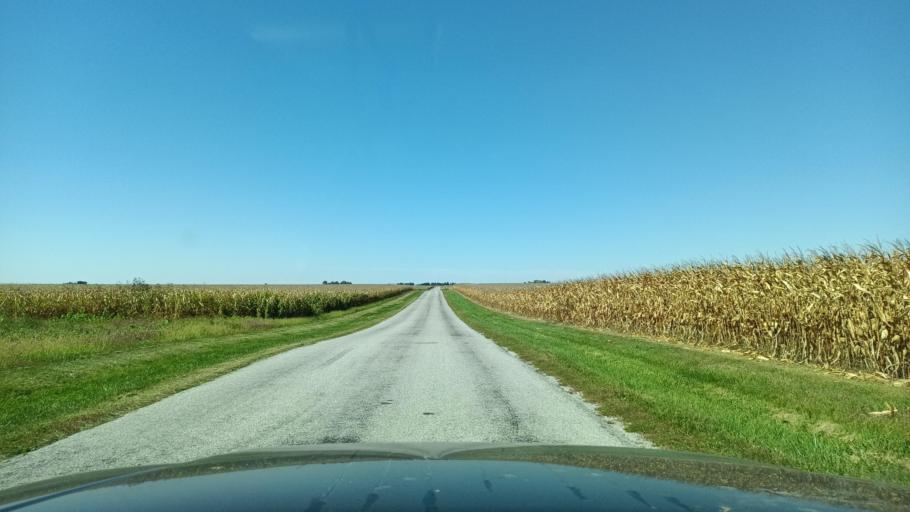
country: US
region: Illinois
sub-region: Champaign County
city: Champaign
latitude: 40.0987
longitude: -88.3376
